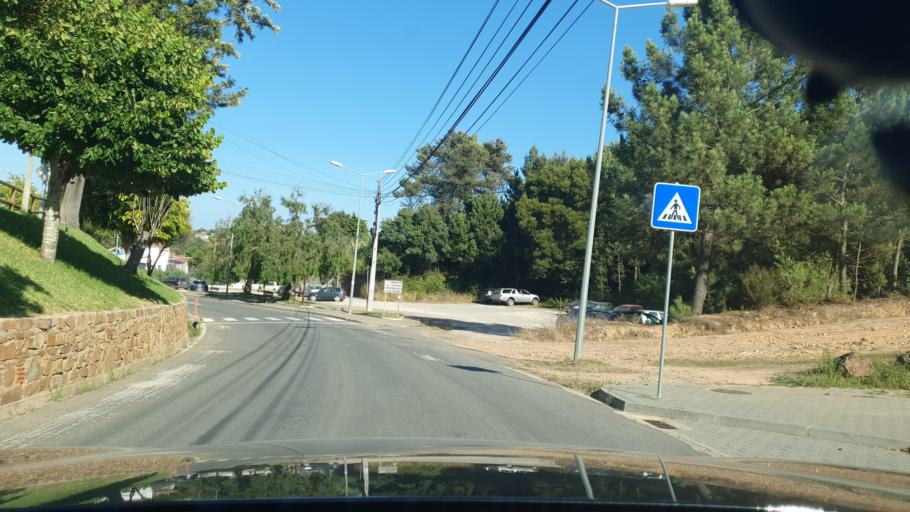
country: PT
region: Beja
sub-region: Odemira
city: Sao Teotonio
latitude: 37.5084
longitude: -8.7091
